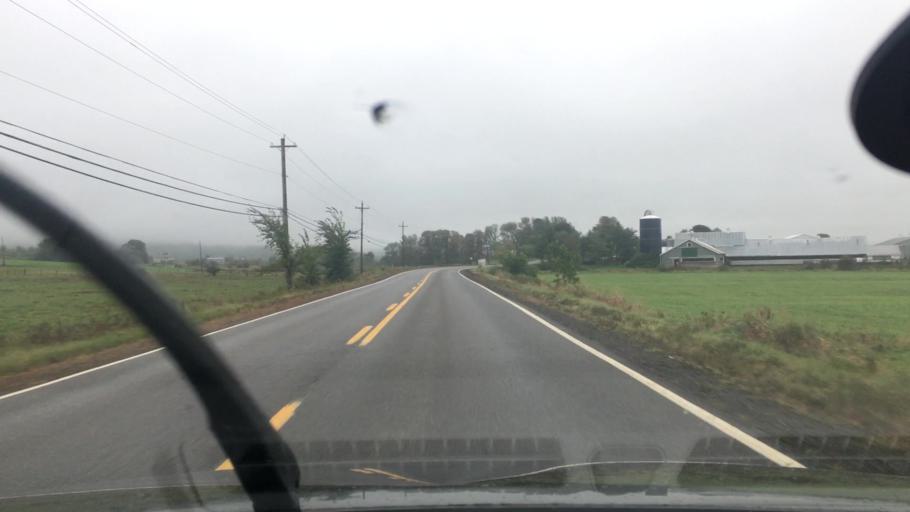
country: CA
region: Nova Scotia
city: Windsor
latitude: 44.9713
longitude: -64.1396
